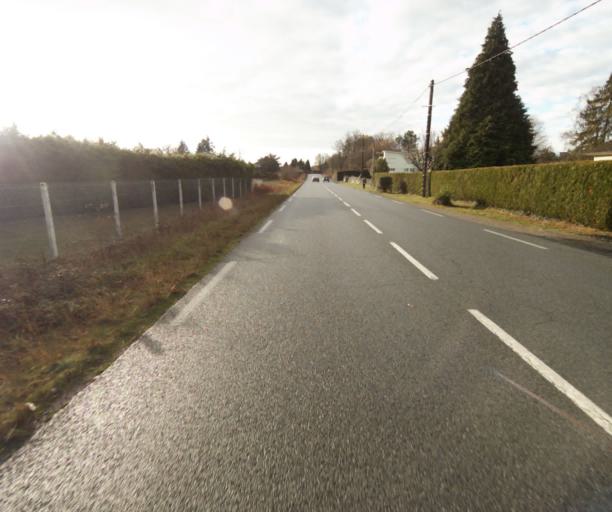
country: FR
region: Limousin
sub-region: Departement de la Correze
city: Saint-Mexant
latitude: 45.2592
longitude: 1.6352
